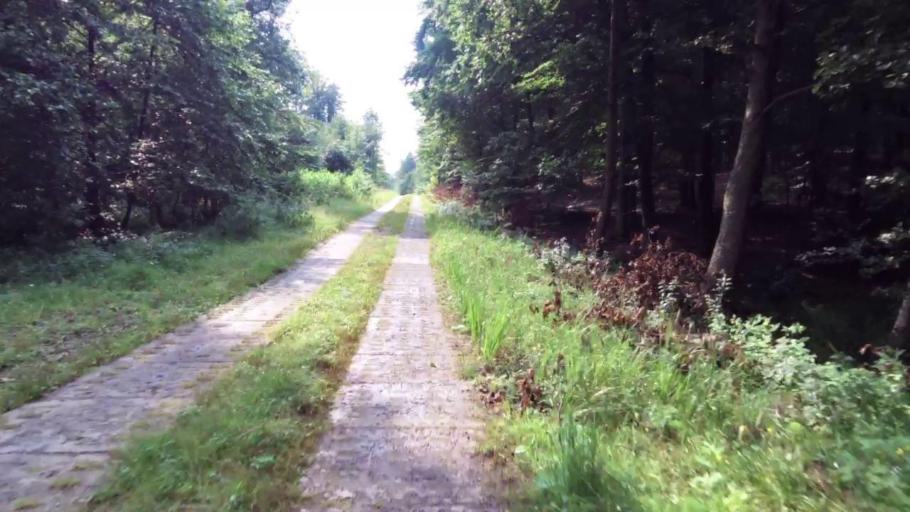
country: PL
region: West Pomeranian Voivodeship
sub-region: Powiat drawski
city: Czaplinek
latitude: 53.6005
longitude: 16.2914
